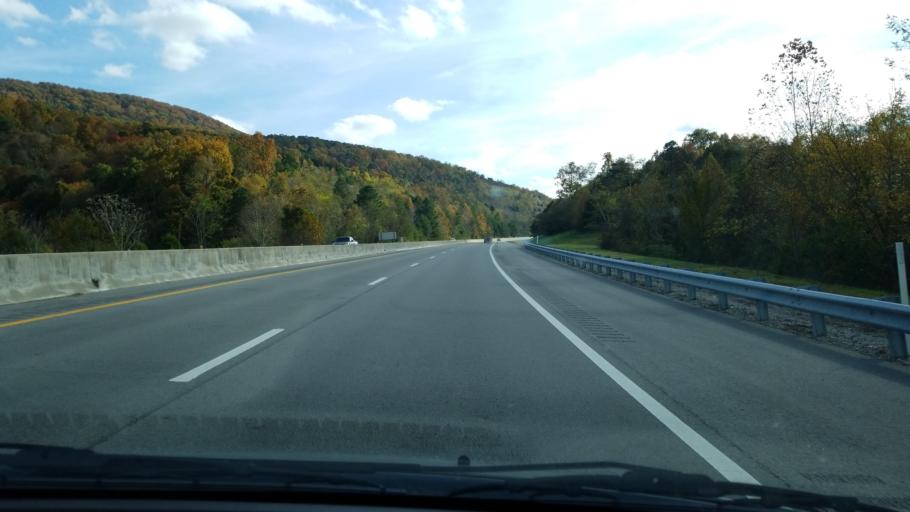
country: US
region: Tennessee
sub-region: Sequatchie County
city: Dunlap
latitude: 35.3855
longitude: -85.3308
